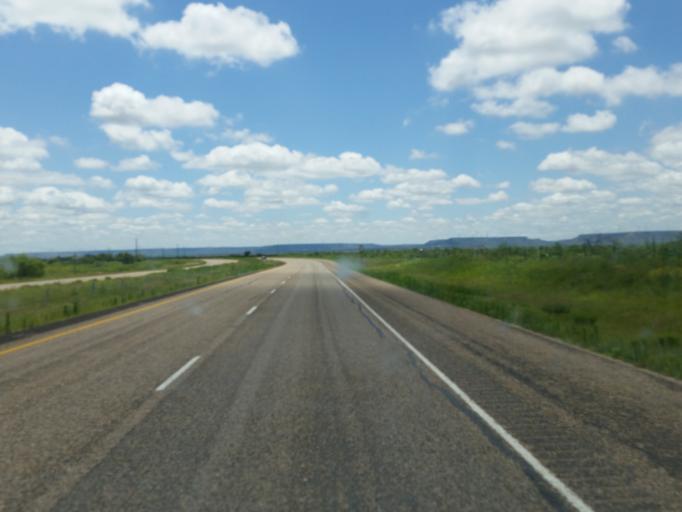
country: US
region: Texas
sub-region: Garza County
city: Post
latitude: 33.0771
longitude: -101.2384
